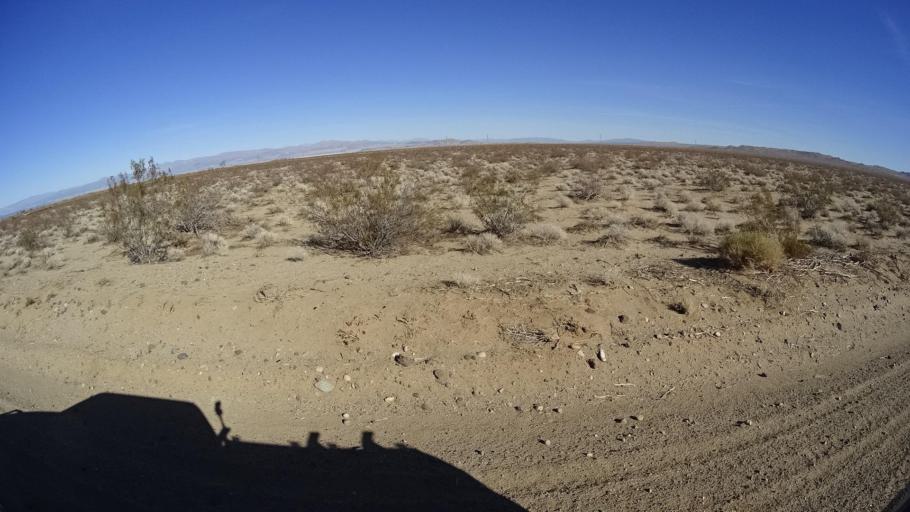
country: US
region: California
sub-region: Kern County
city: China Lake Acres
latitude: 35.5859
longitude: -117.7904
